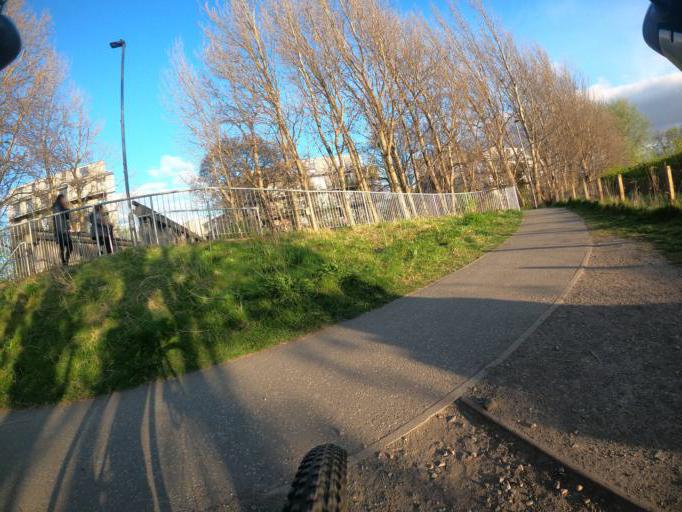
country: GB
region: Scotland
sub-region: Edinburgh
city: Colinton
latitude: 55.9386
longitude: -3.2460
